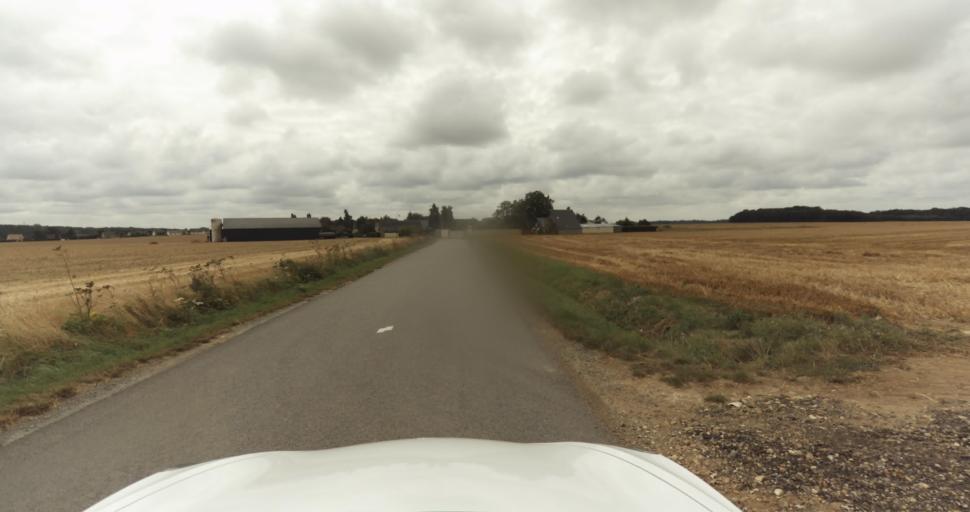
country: FR
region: Haute-Normandie
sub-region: Departement de l'Eure
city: Claville
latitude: 49.0319
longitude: 1.0303
